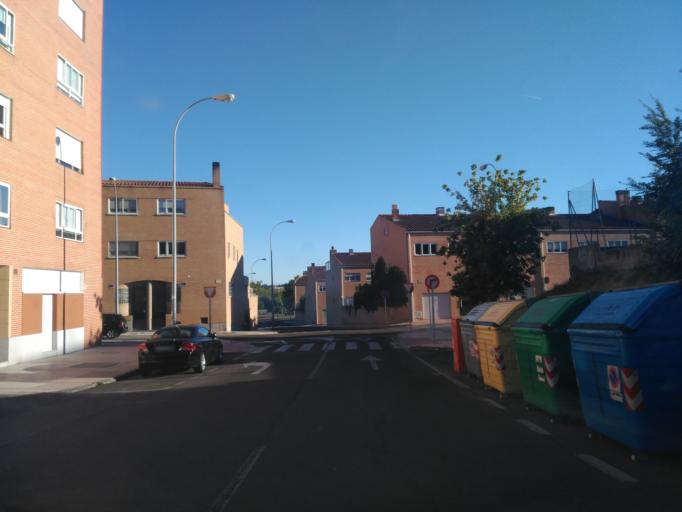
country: ES
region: Castille and Leon
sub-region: Provincia de Salamanca
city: Salamanca
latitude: 40.9666
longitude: -5.6455
